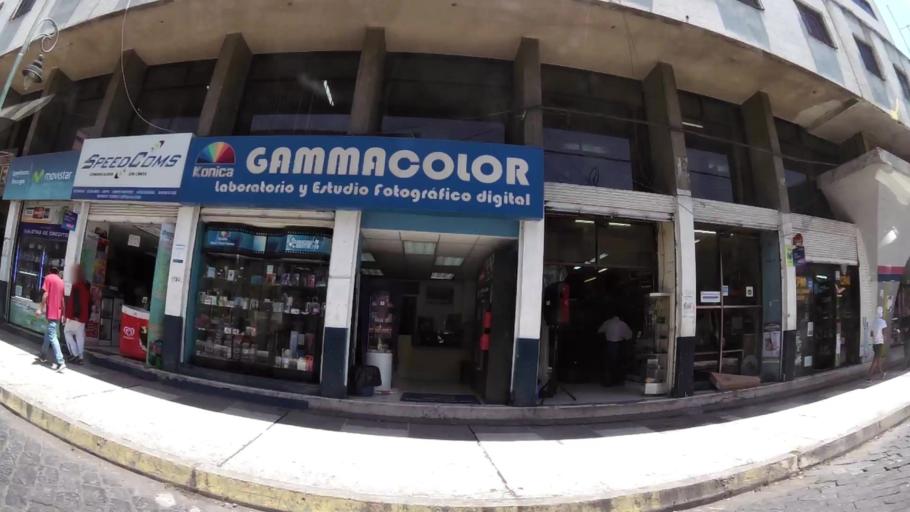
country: EC
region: Chimborazo
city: Riobamba
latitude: -1.6717
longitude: -78.6511
